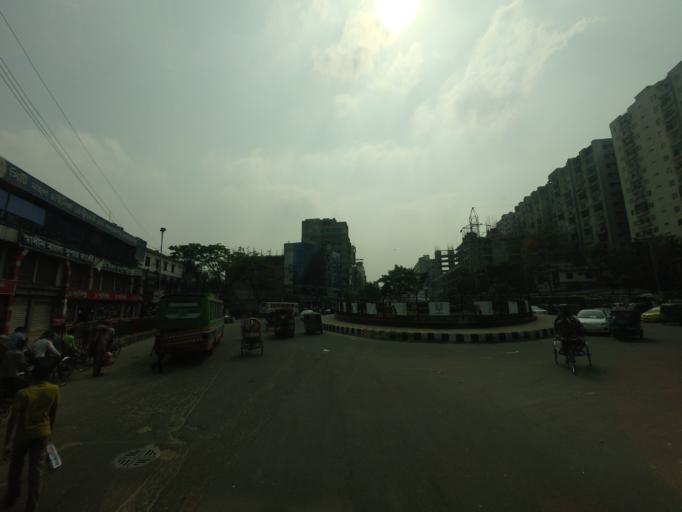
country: BD
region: Dhaka
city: Azimpur
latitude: 23.8001
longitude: 90.3557
